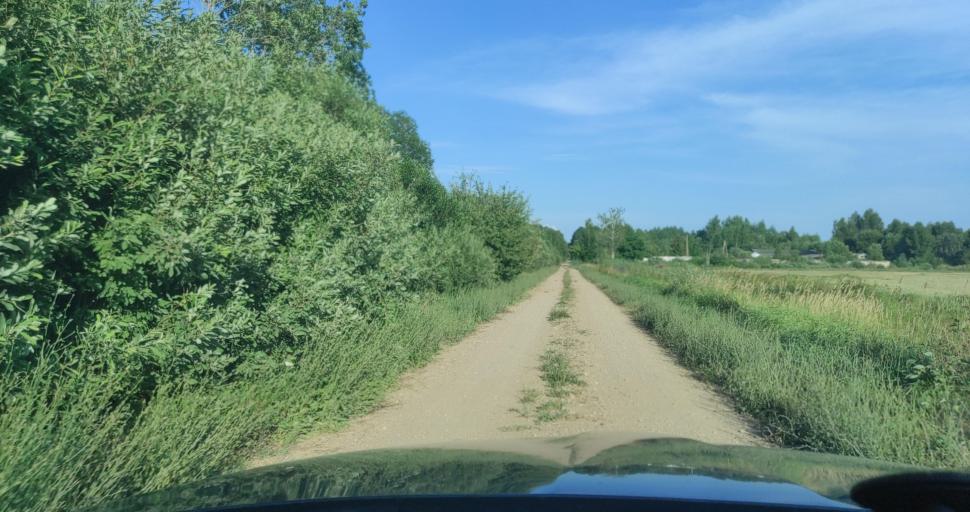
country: LV
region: Skrunda
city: Skrunda
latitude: 56.6763
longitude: 21.9887
